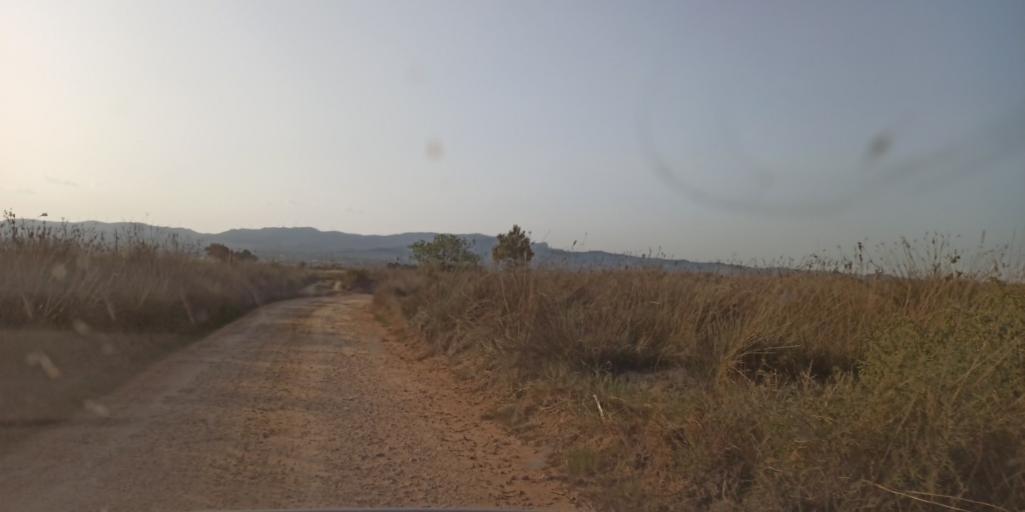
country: ES
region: Catalonia
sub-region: Provincia de Tarragona
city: L'Ampolla
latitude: 40.7816
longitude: 0.7140
